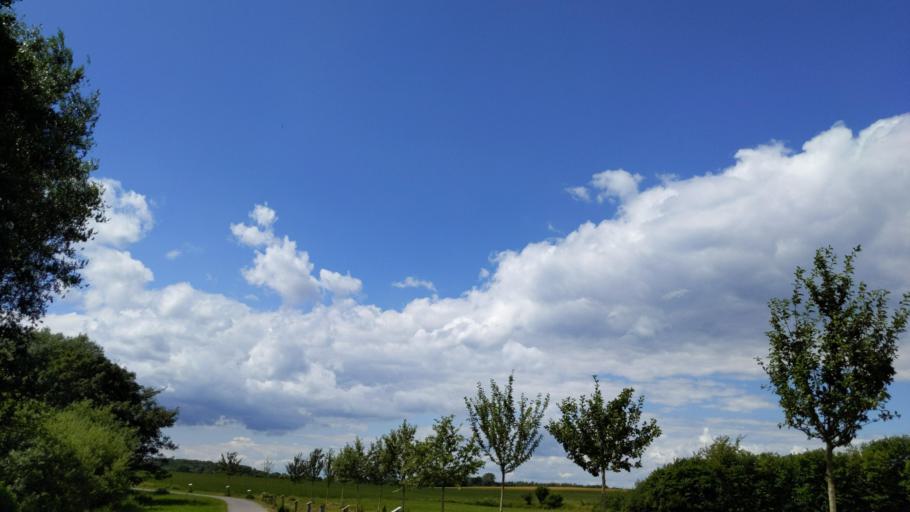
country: DE
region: Mecklenburg-Vorpommern
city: Kalkhorst
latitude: 54.0024
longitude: 11.0785
